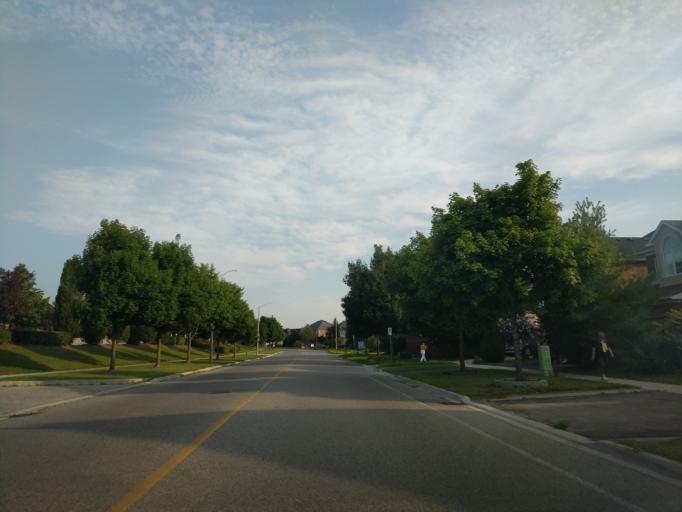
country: CA
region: Ontario
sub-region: York
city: Richmond Hill
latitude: 43.8830
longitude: -79.4024
